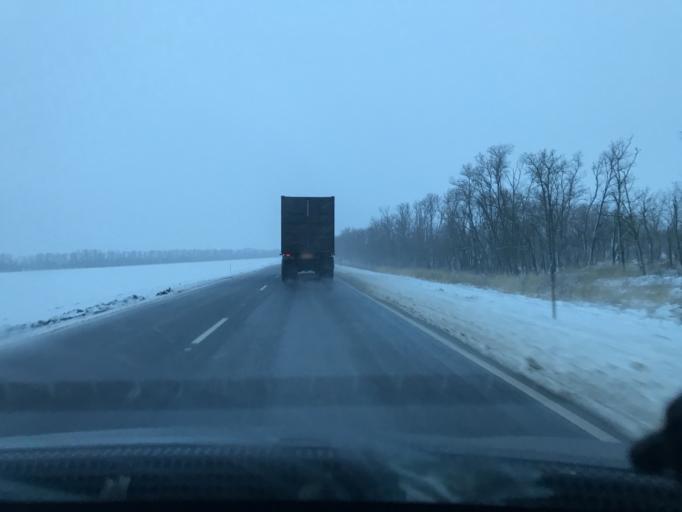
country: RU
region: Rostov
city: Letnik
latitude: 46.0721
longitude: 41.1997
